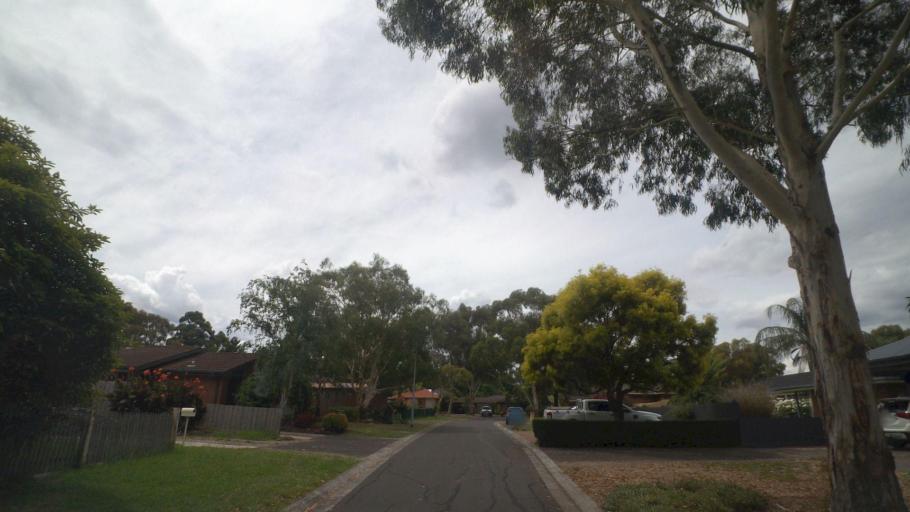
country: AU
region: Victoria
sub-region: Maroondah
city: Bayswater North
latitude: -37.8189
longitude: 145.2845
